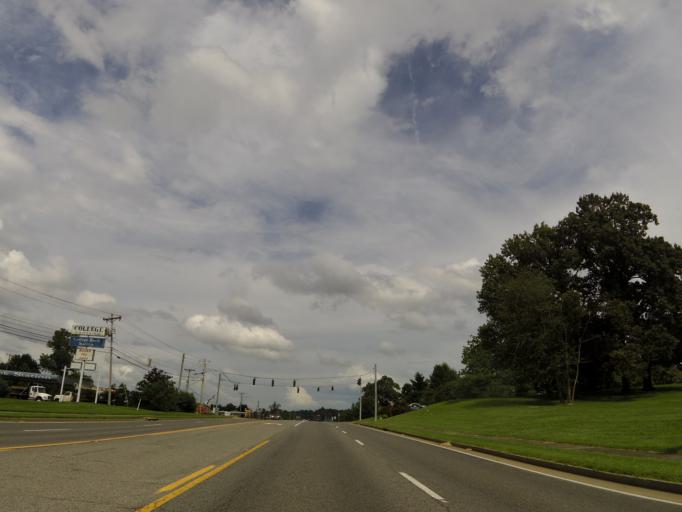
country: US
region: Kentucky
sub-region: McCracken County
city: Hendron
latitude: 37.0554
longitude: -88.6617
